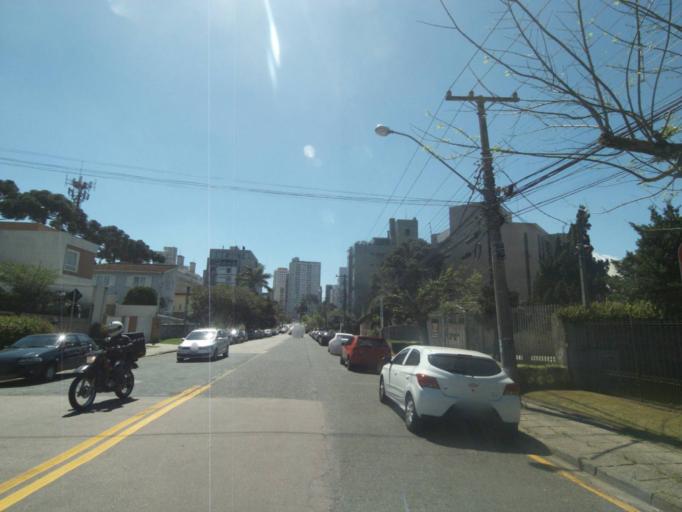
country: BR
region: Parana
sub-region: Curitiba
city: Curitiba
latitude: -25.4113
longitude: -49.2508
